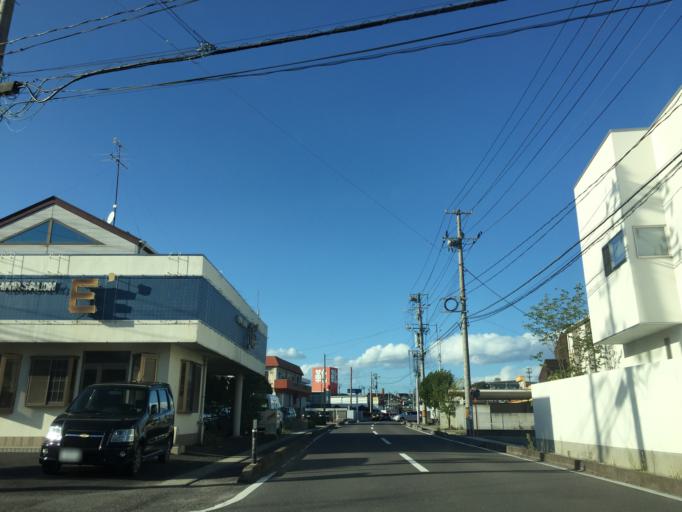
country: JP
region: Fukushima
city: Koriyama
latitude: 37.4165
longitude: 140.3588
